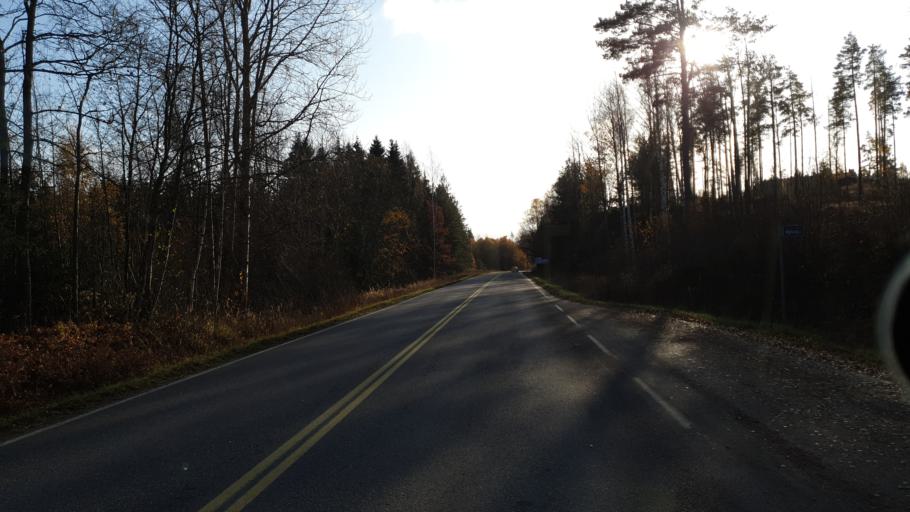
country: FI
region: Uusimaa
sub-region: Helsinki
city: Siuntio
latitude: 60.1935
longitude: 24.1978
